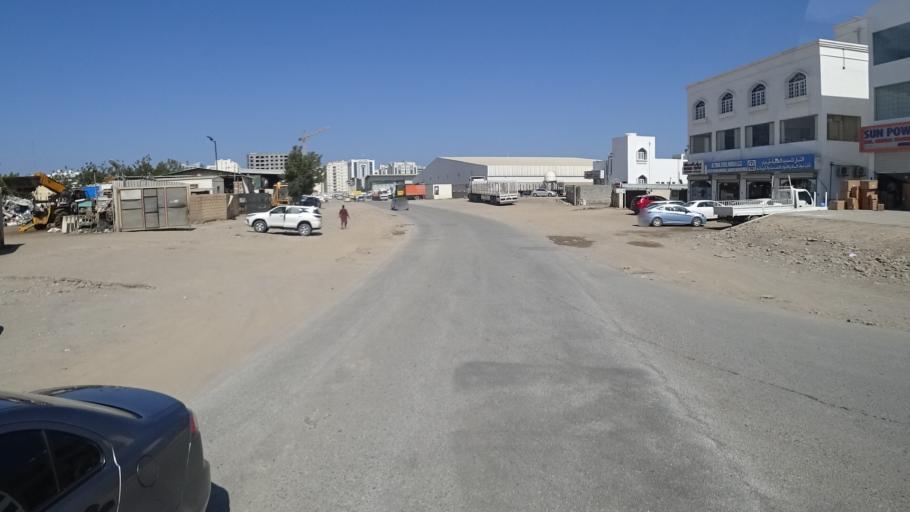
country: OM
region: Muhafazat Masqat
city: Bawshar
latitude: 23.5780
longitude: 58.3685
